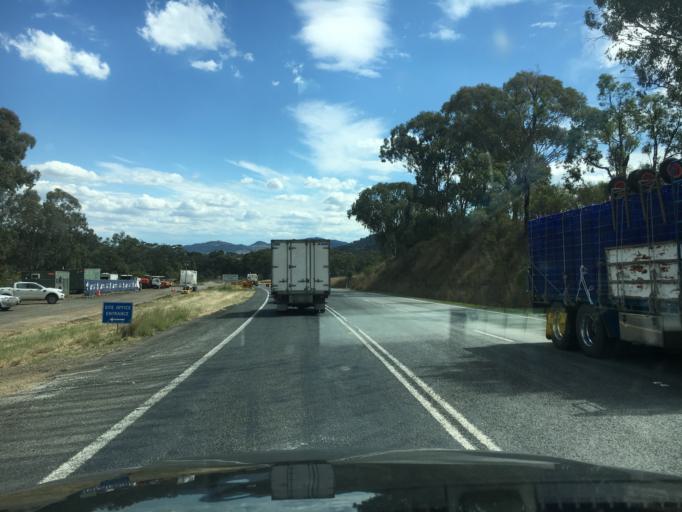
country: AU
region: New South Wales
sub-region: Liverpool Plains
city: Quirindi
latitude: -31.4504
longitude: 150.8646
